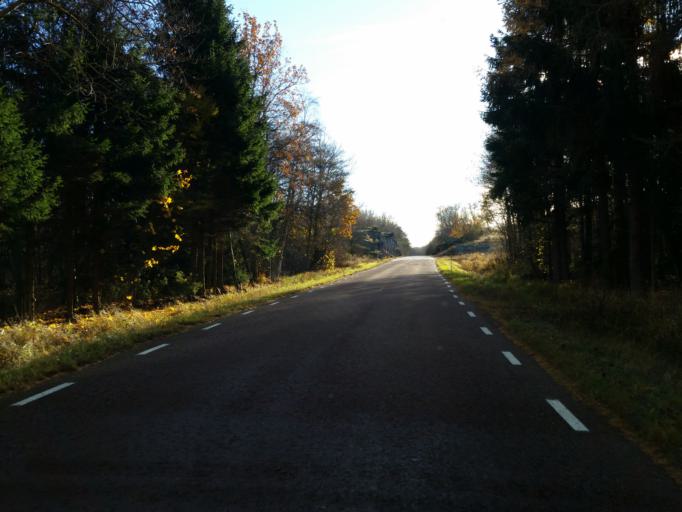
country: AX
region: Alands skaergard
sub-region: Kumlinge
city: Kumlinge
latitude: 60.2332
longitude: 20.7365
